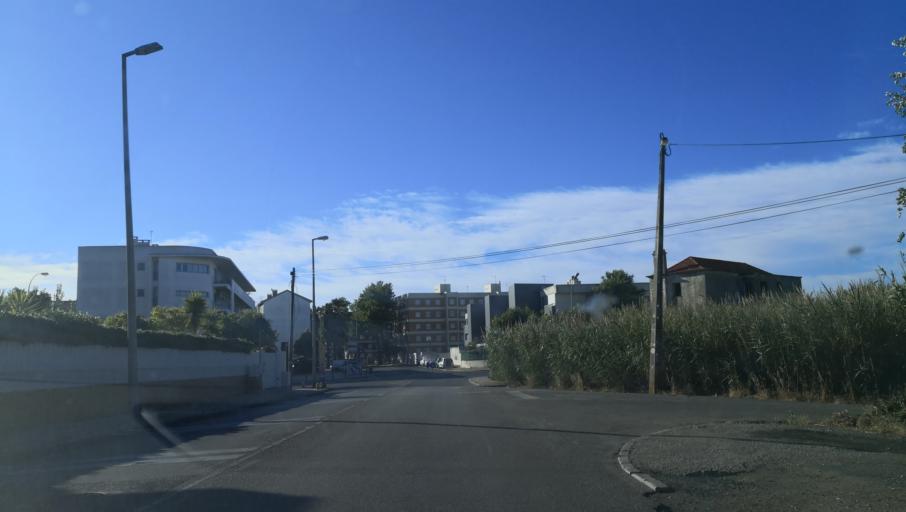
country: PT
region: Lisbon
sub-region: Oeiras
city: Carcavelos
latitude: 38.6838
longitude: -9.3249
